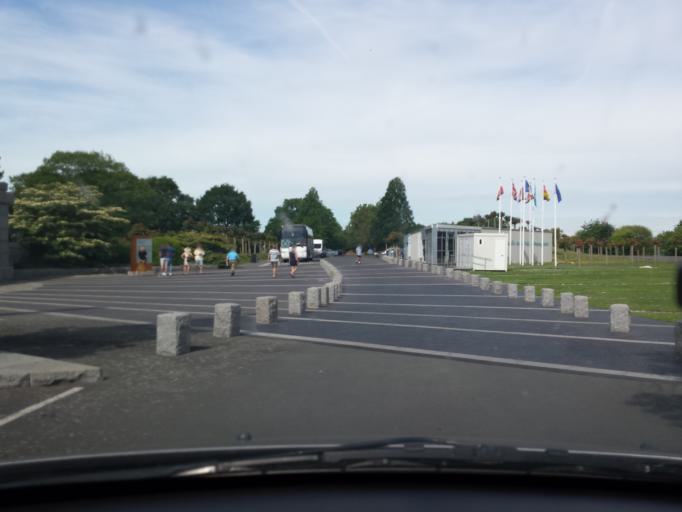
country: FR
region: Lower Normandy
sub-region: Departement du Calvados
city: Grandcamp-Maisy
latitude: 49.3432
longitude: -1.0262
